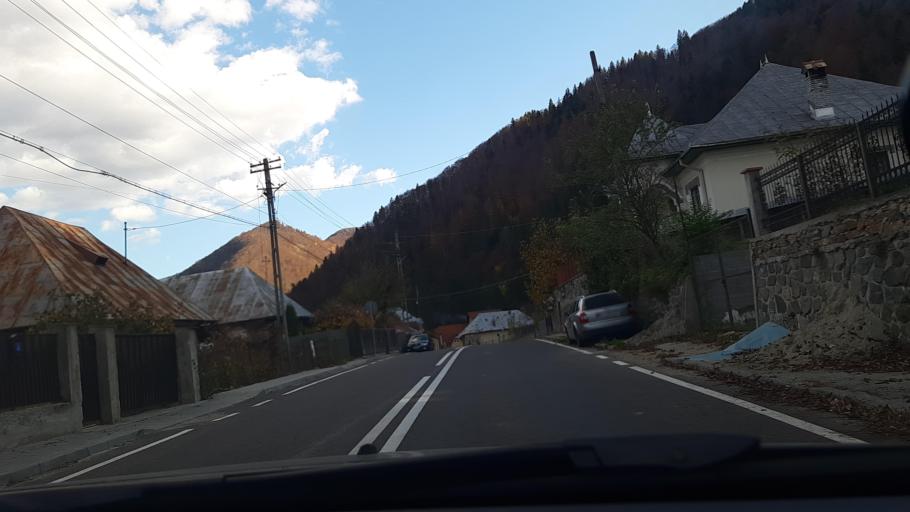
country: RO
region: Valcea
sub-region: Comuna Voineasa
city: Voineasa
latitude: 45.4129
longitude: 23.9630
